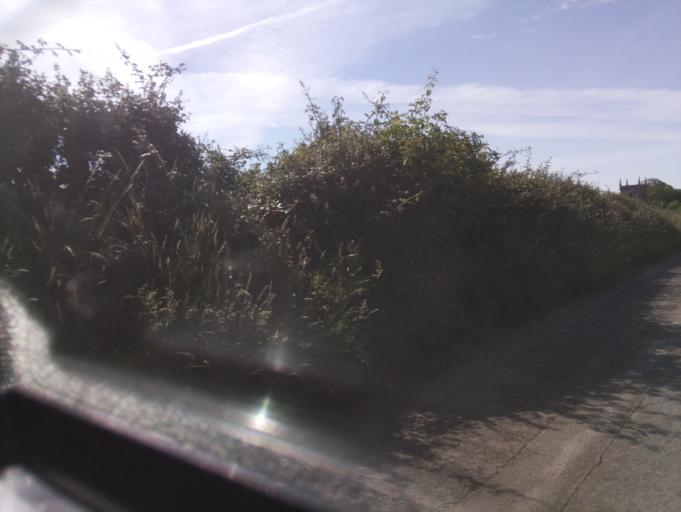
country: GB
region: England
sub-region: Wiltshire
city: Nettleton
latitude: 51.4756
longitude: -2.2642
